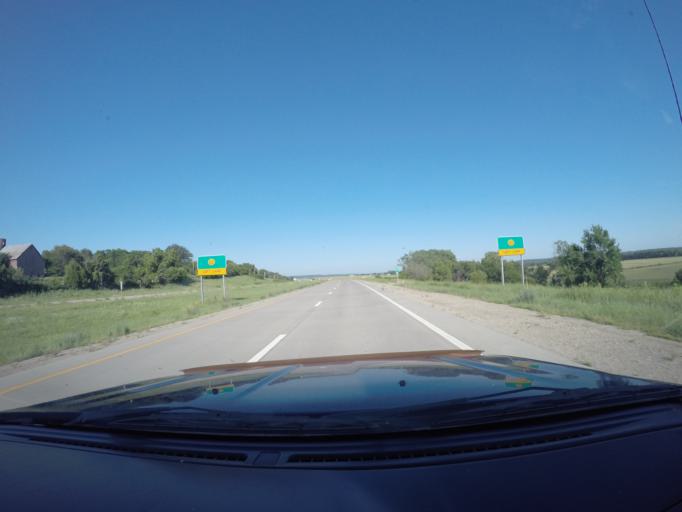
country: US
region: Kansas
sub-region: Shawnee County
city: Topeka
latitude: 39.0866
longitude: -95.4852
